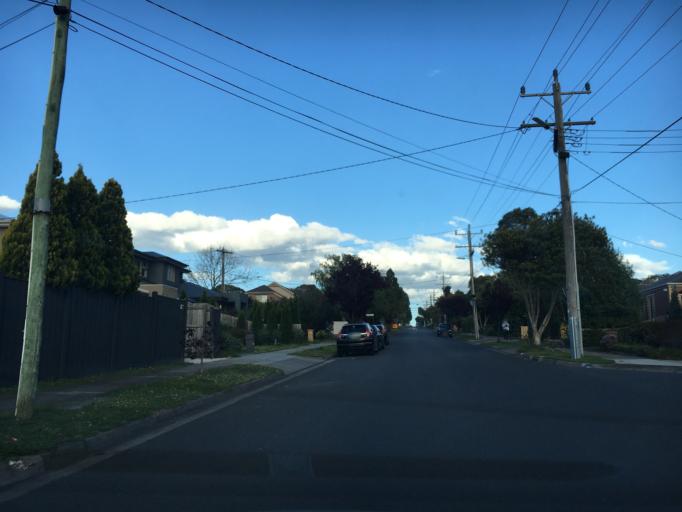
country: AU
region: Victoria
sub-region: Monash
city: Notting Hill
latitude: -37.8855
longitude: 145.1676
